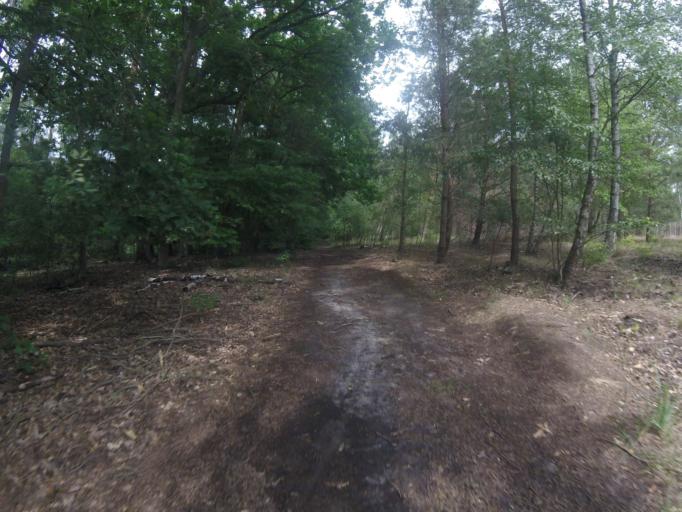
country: DE
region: Brandenburg
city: Konigs Wusterhausen
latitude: 52.2757
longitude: 13.6115
